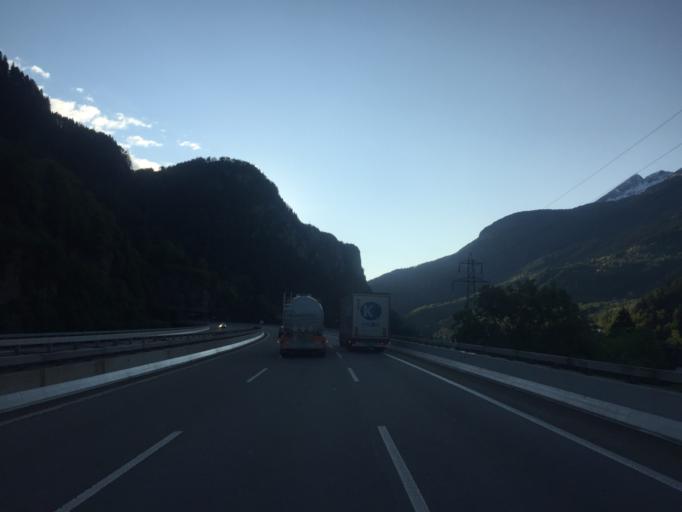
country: CH
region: Ticino
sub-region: Leventina District
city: Faido
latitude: 46.4737
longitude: 8.8058
